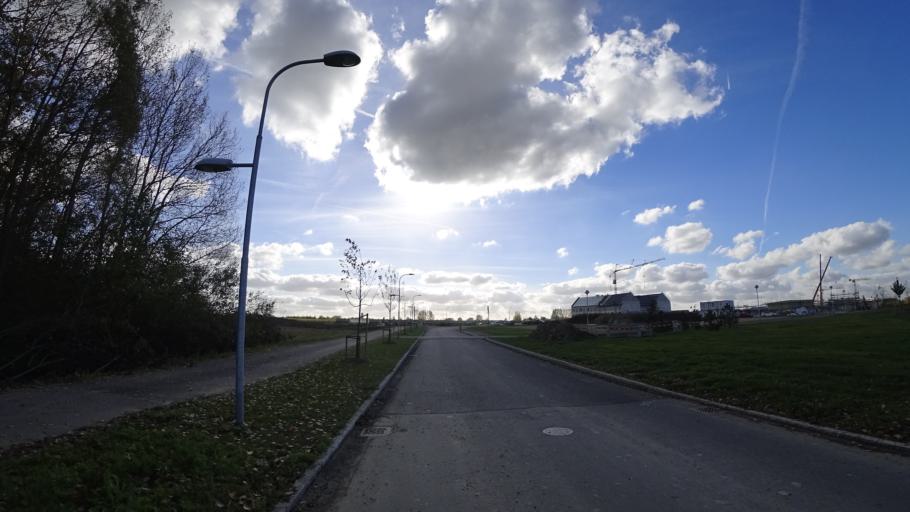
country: SE
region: Skane
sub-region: Staffanstorps Kommun
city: Staffanstorp
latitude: 55.6326
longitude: 13.2100
